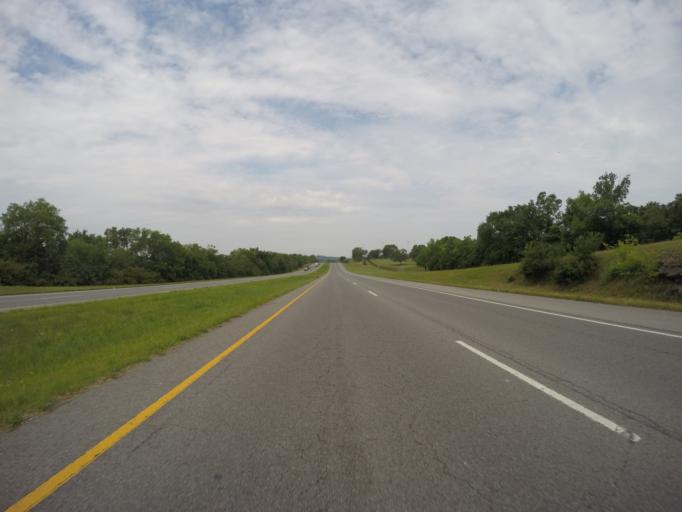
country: US
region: Tennessee
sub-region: Davidson County
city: Goodlettsville
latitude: 36.2644
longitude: -86.6972
